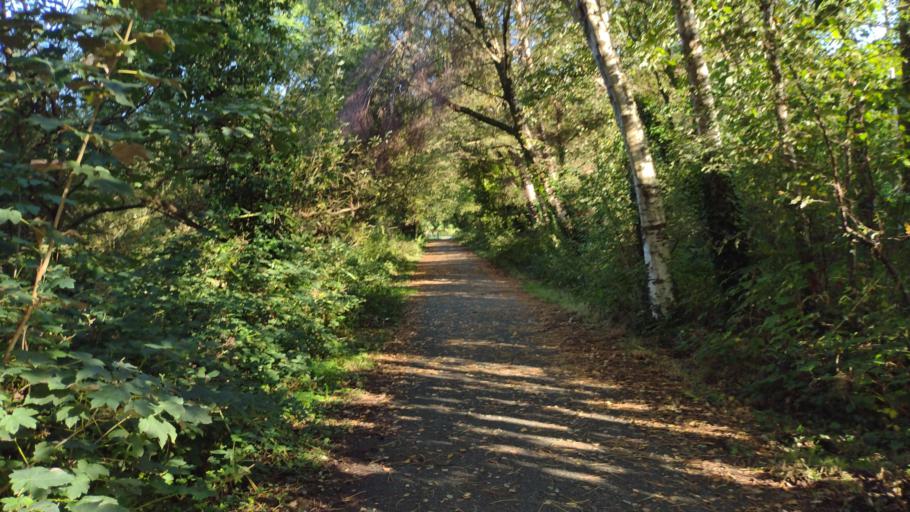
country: GB
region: Wales
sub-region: Gwynedd
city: Barmouth
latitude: 52.7068
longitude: -4.0301
